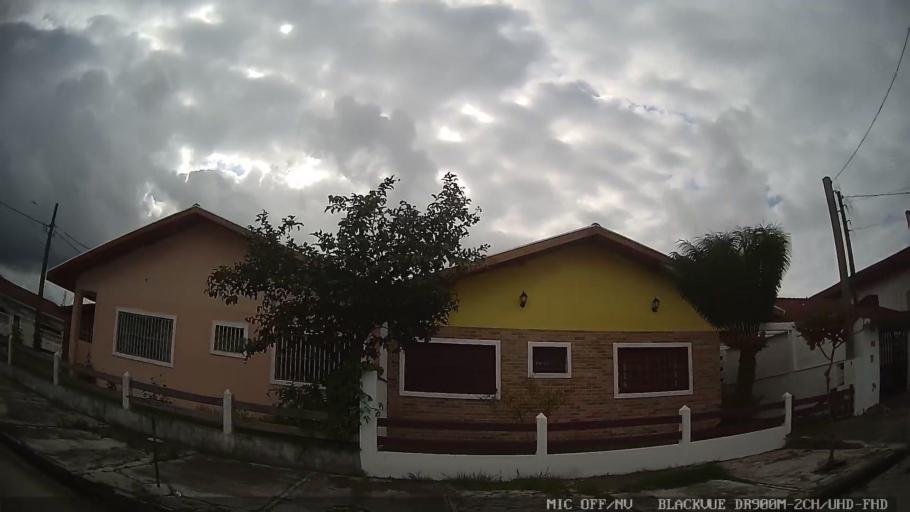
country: BR
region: Sao Paulo
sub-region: Itanhaem
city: Itanhaem
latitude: -24.1975
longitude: -46.8215
